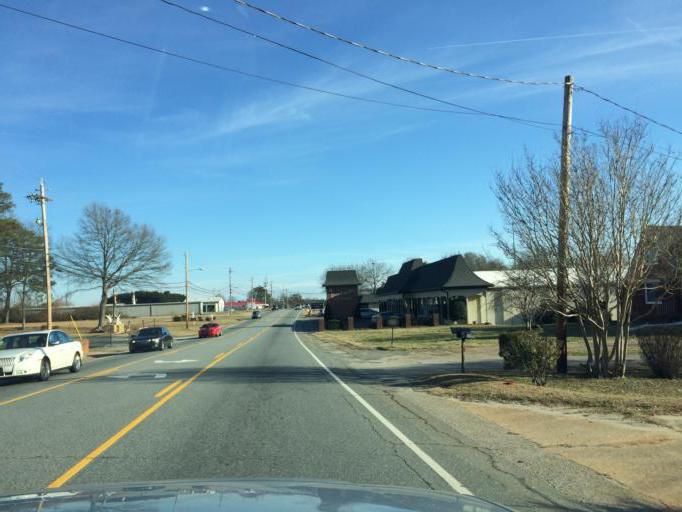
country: US
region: North Carolina
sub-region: Rutherford County
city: Forest City
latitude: 35.3495
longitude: -81.8895
